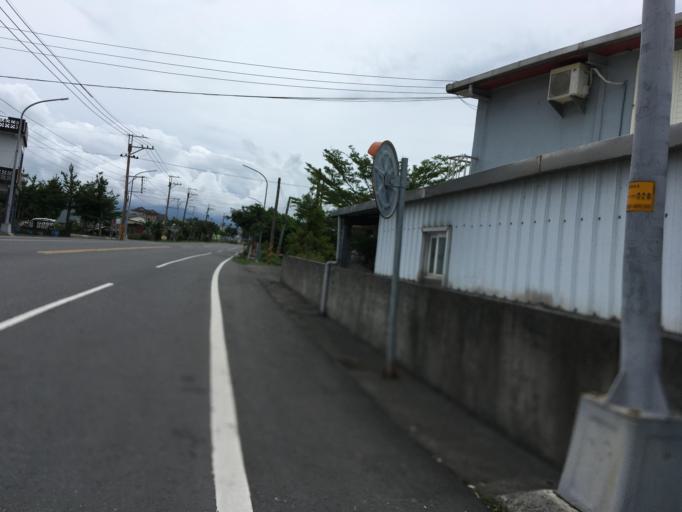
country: TW
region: Taiwan
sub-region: Yilan
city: Yilan
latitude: 24.6915
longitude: 121.8069
